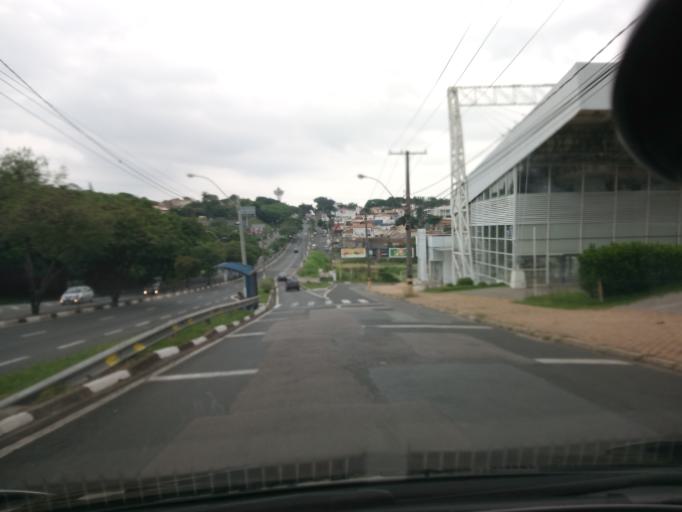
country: BR
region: Sao Paulo
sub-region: Campinas
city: Campinas
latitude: -22.9035
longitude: -47.0321
